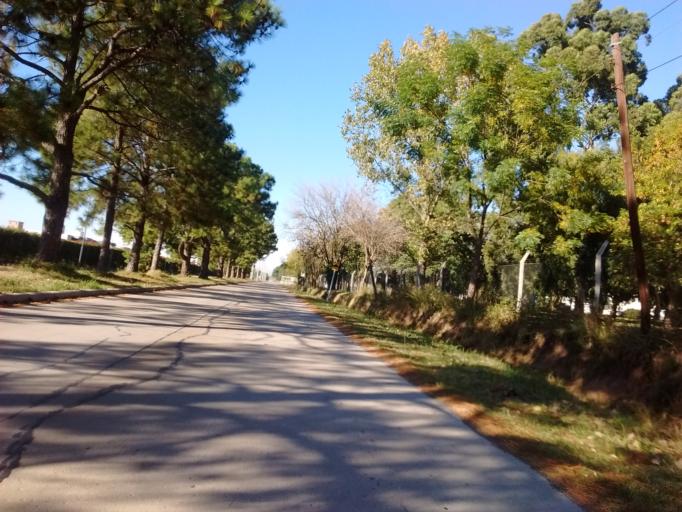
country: AR
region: Santa Fe
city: Funes
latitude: -32.9327
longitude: -60.8120
